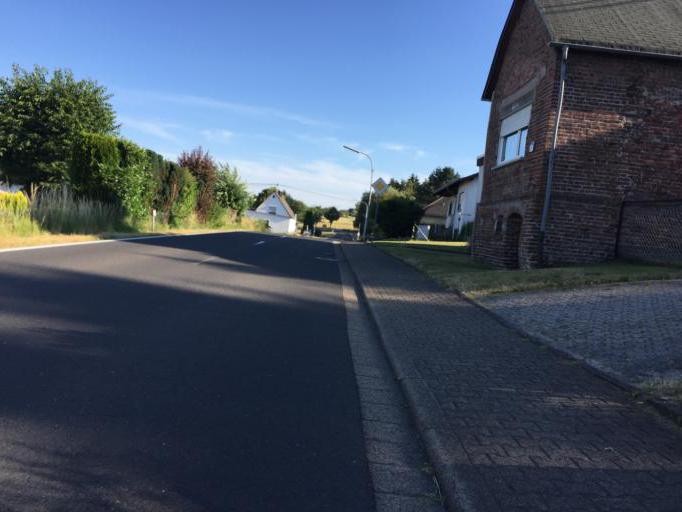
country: DE
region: Rheinland-Pfalz
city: Kaden
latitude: 50.5459
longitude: 7.9135
